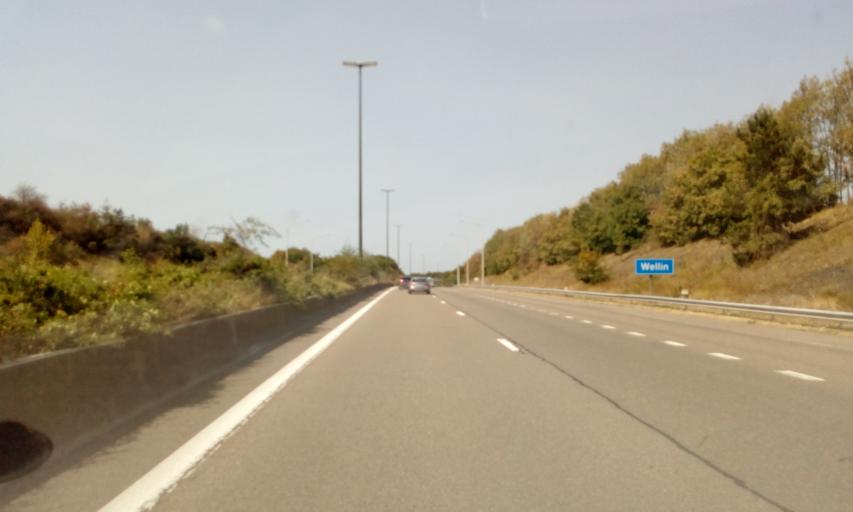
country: BE
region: Wallonia
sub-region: Province du Luxembourg
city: Wellin
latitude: 50.0931
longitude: 5.1431
